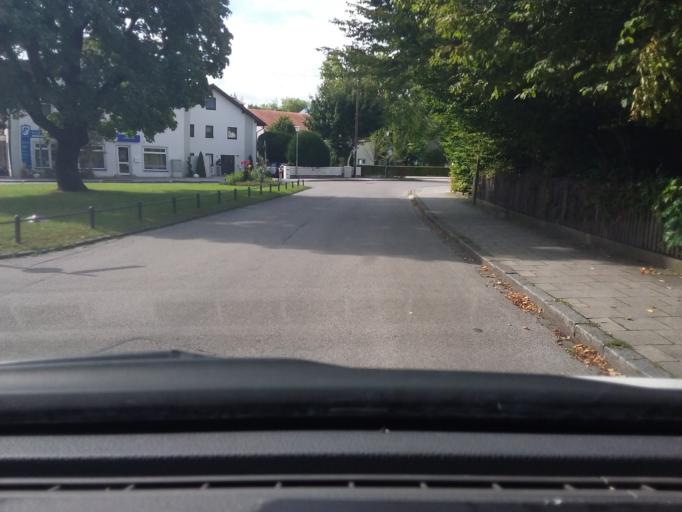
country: DE
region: Bavaria
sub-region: Upper Bavaria
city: Ismaning
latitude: 48.2250
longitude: 11.6774
